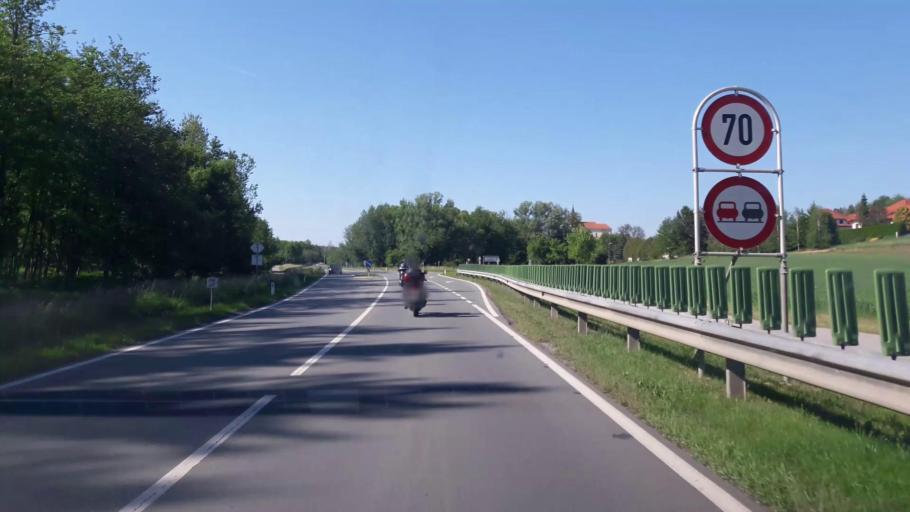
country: AT
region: Burgenland
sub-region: Politischer Bezirk Oberwart
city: Litzelsdorf
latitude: 47.2017
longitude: 16.1607
